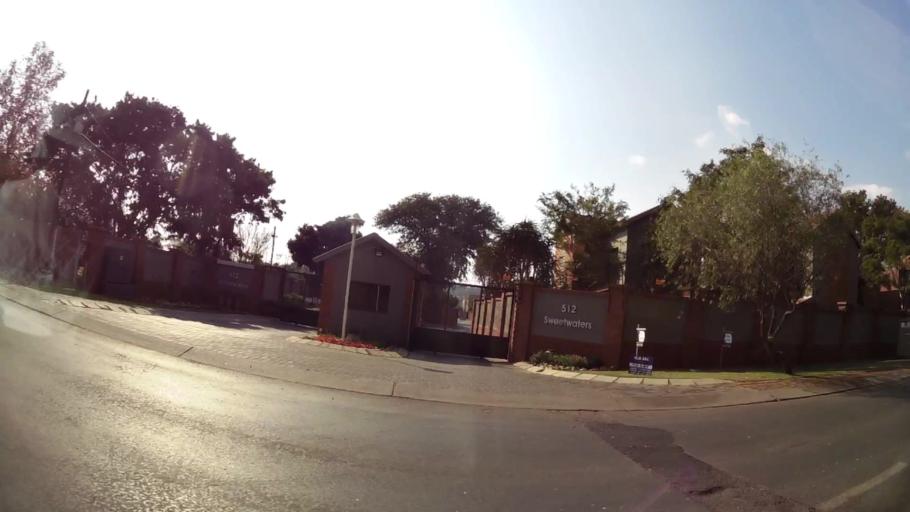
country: ZA
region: Gauteng
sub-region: City of Tshwane Metropolitan Municipality
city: Pretoria
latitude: -25.7705
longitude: 28.3441
